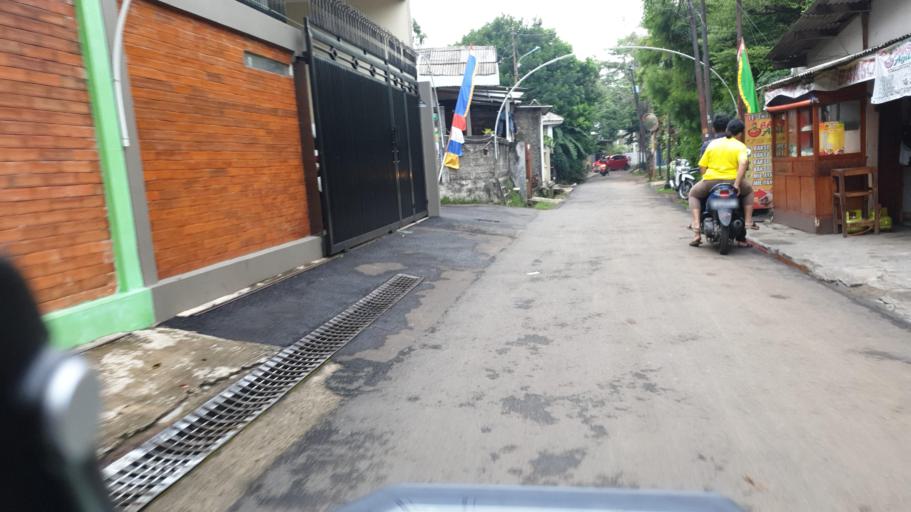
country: ID
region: West Java
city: Depok
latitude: -6.3444
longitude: 106.8245
